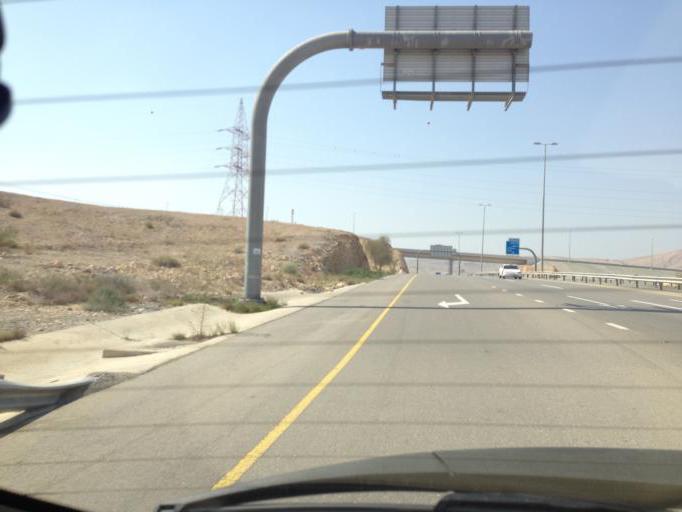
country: OM
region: Muhafazat Masqat
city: As Sib al Jadidah
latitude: 23.5708
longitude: 58.1913
